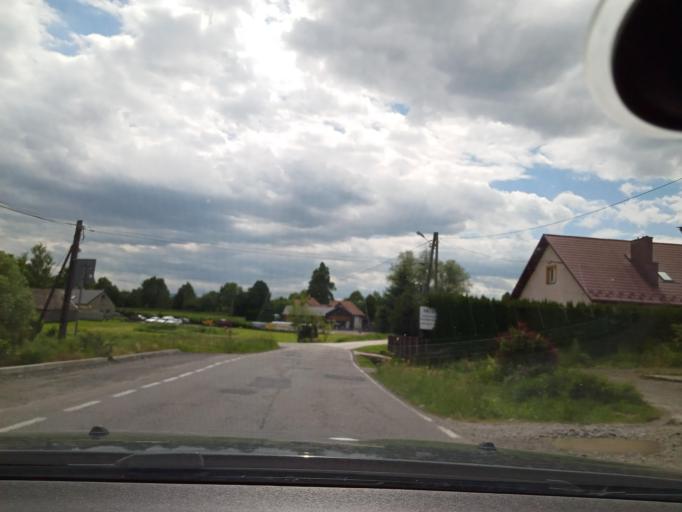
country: PL
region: Lesser Poland Voivodeship
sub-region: Powiat bochenski
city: Lapanow
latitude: 49.8562
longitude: 20.2516
